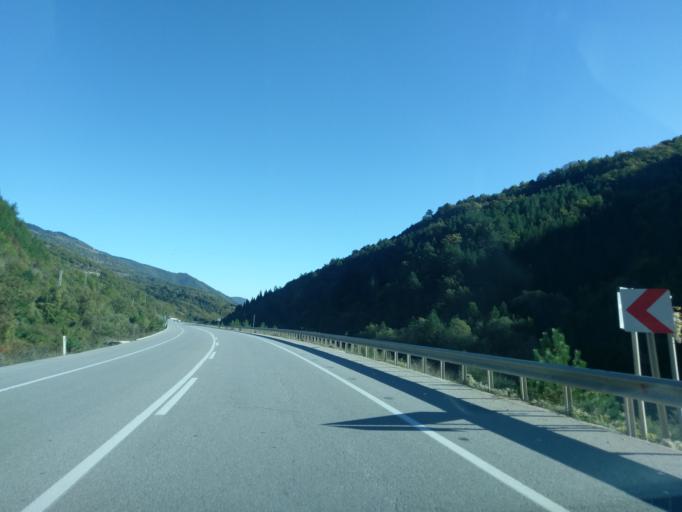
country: TR
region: Sinop
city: Erfelek
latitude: 41.7140
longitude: 34.9337
